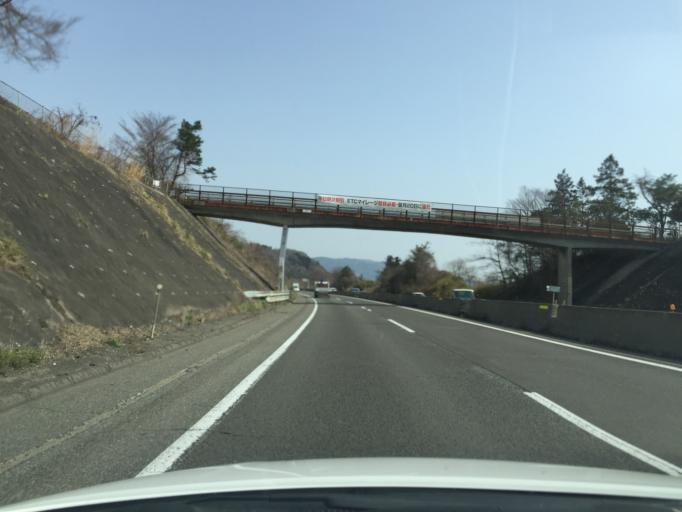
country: JP
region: Fukushima
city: Hobaramachi
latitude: 37.8431
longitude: 140.5044
